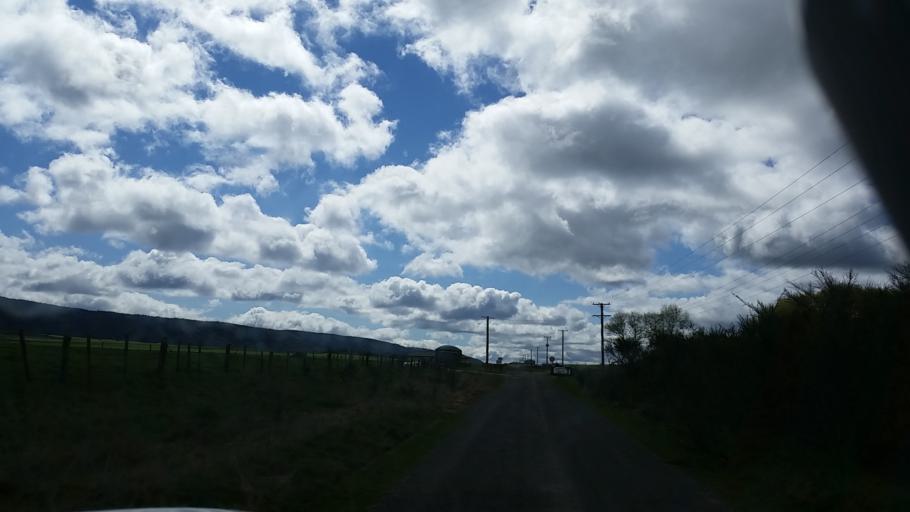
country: NZ
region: Bay of Plenty
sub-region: Kawerau District
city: Kawerau
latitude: -38.2824
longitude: 176.5520
